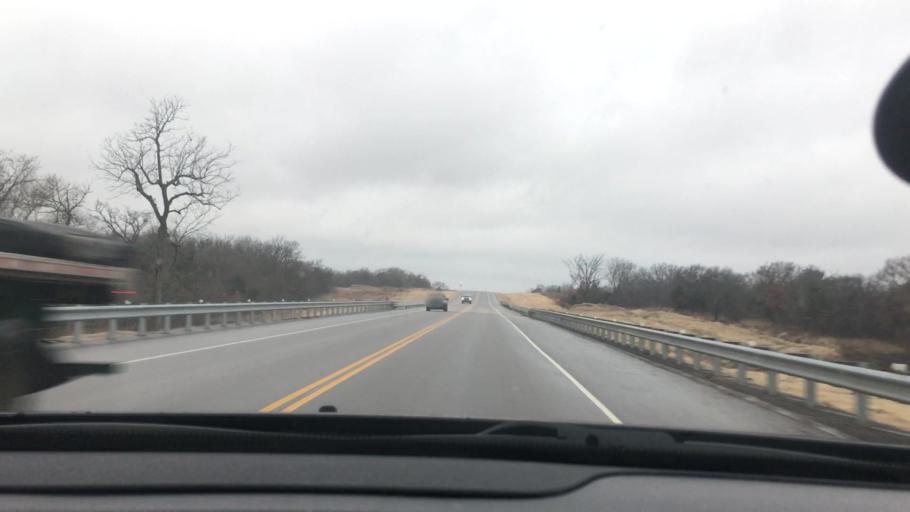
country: US
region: Oklahoma
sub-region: Johnston County
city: Tishomingo
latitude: 34.3301
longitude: -96.6570
